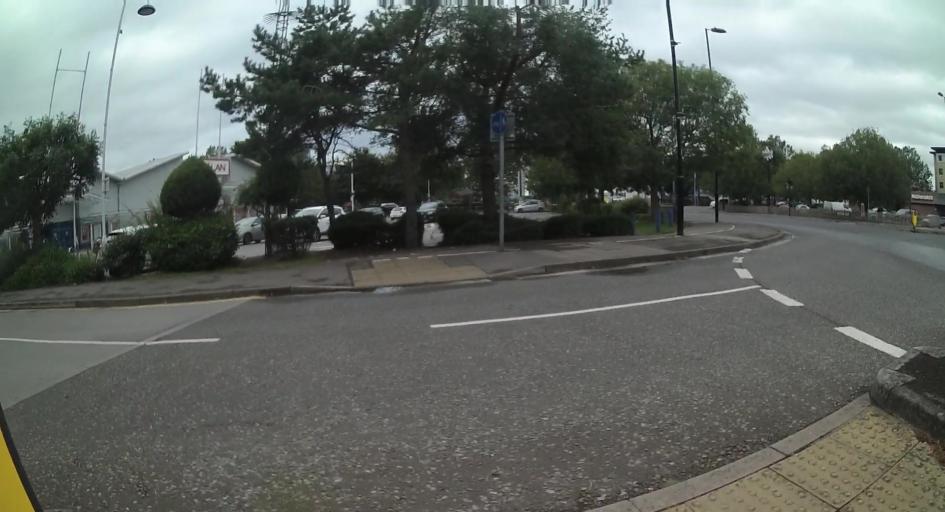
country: GB
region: England
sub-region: Southampton
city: Southampton
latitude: 50.9048
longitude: -1.4127
